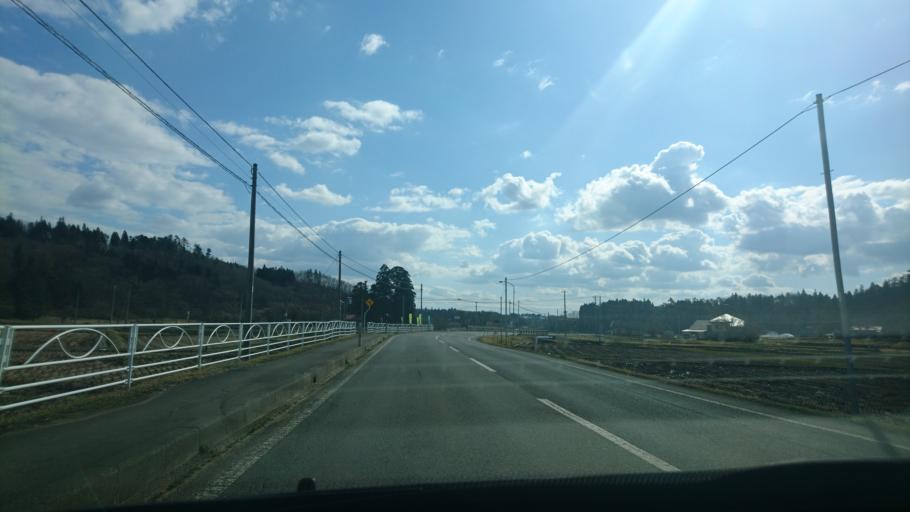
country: JP
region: Iwate
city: Kitakami
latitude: 39.2418
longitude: 141.2014
